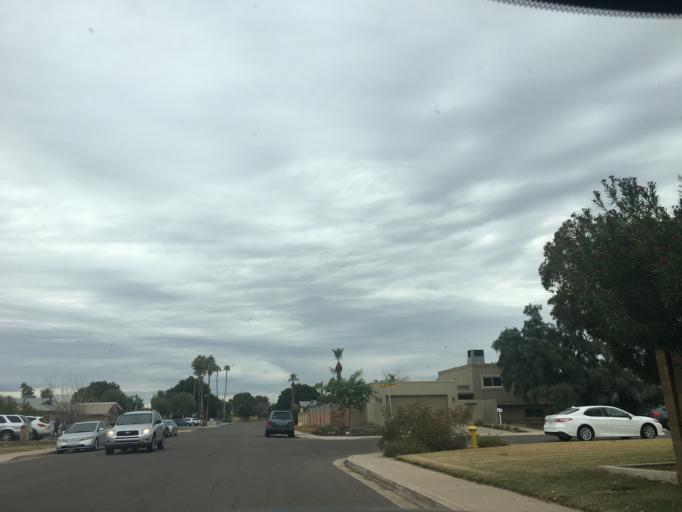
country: US
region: Arizona
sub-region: Maricopa County
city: Tempe
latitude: 33.3809
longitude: -111.9174
